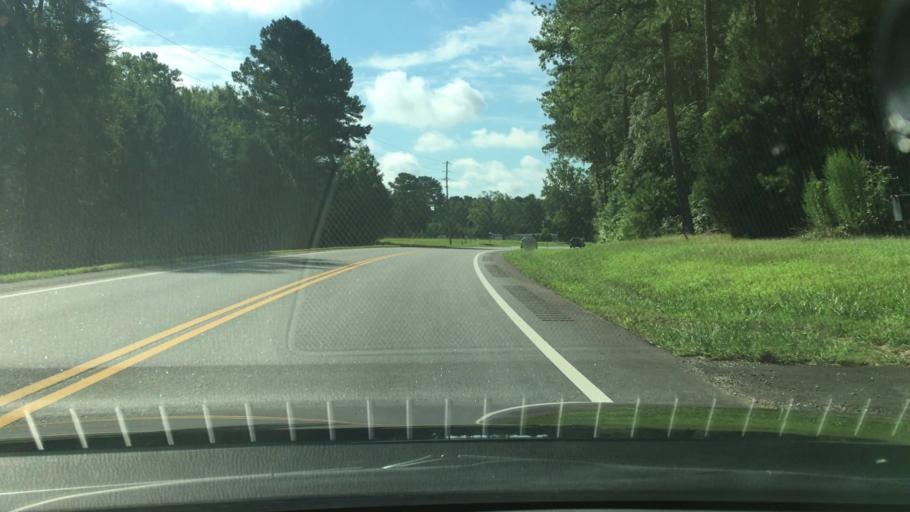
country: US
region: Georgia
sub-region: Morgan County
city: Madison
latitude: 33.5304
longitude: -83.4460
